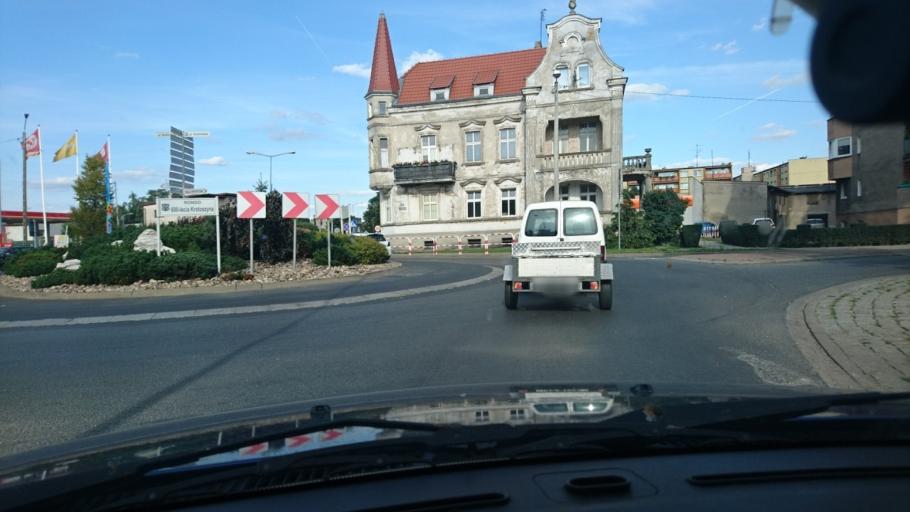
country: PL
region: Greater Poland Voivodeship
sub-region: Powiat krotoszynski
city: Krotoszyn
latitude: 51.7010
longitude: 17.4381
